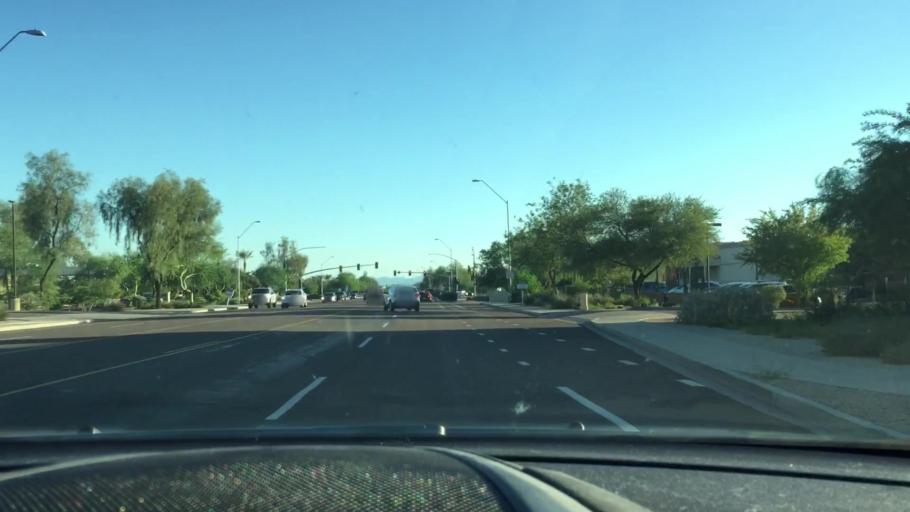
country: US
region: Arizona
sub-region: Maricopa County
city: Sun City
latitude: 33.6834
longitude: -112.2379
